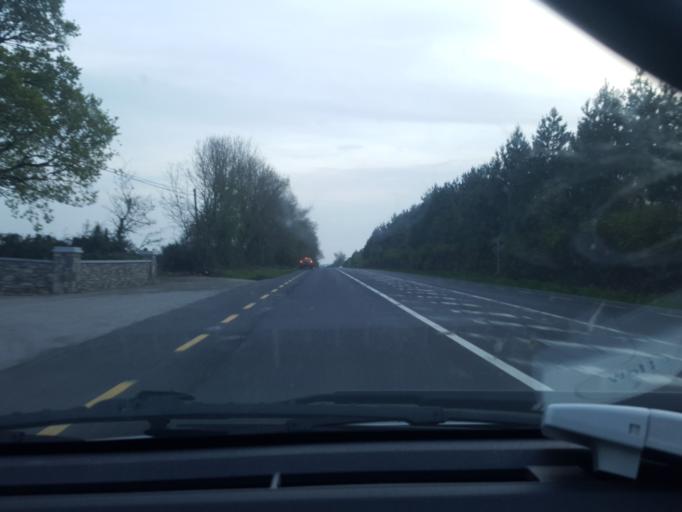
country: IE
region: Munster
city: Cahir
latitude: 52.3659
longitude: -7.9681
